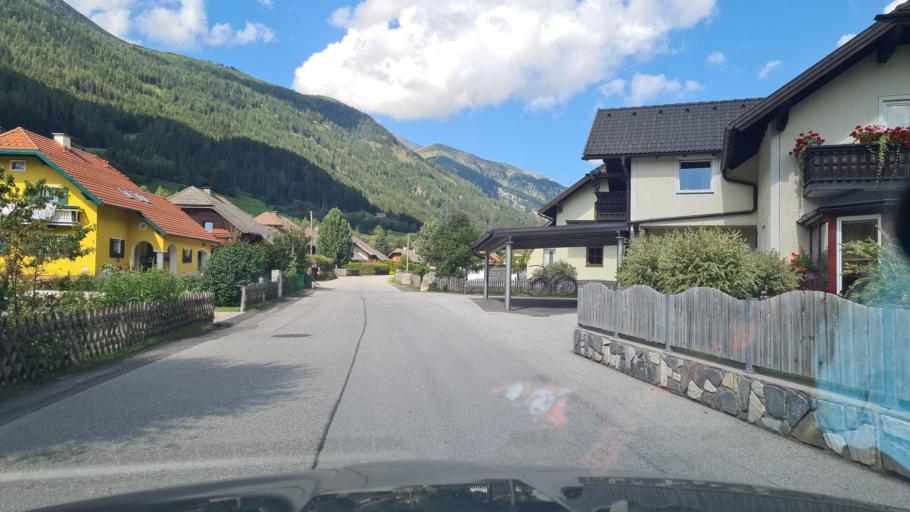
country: AT
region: Salzburg
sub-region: Politischer Bezirk Tamsweg
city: Zederhaus
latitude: 47.1602
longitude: 13.4895
